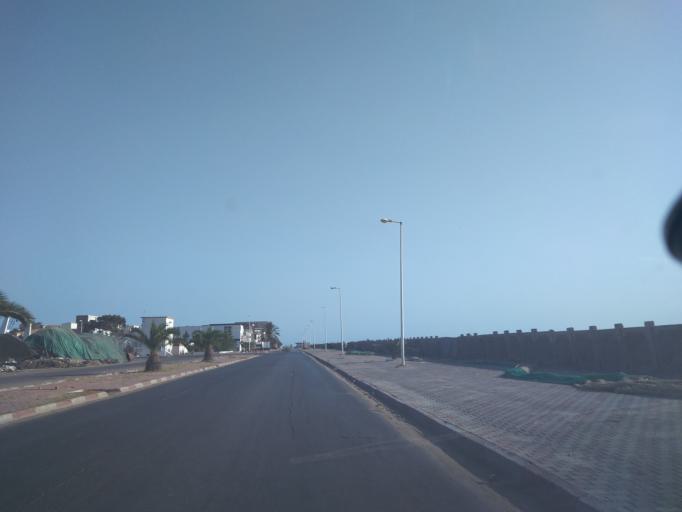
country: TN
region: Safaqis
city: Sfax
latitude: 34.7166
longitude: 10.7608
